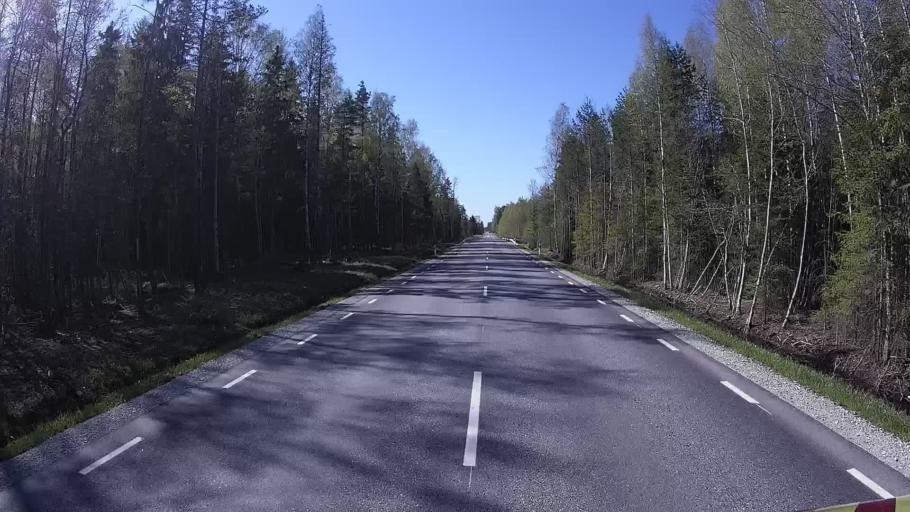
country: EE
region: Raplamaa
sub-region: Jaervakandi vald
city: Jarvakandi
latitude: 58.7289
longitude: 24.8022
